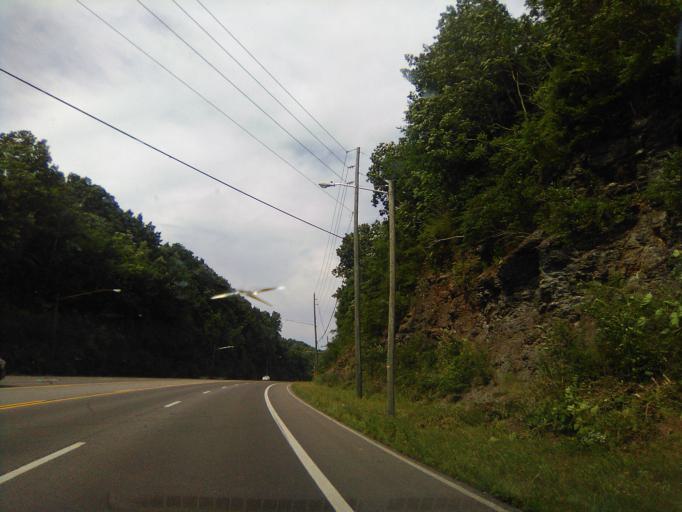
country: US
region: Tennessee
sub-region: Davidson County
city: Belle Meade
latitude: 36.0820
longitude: -86.8977
